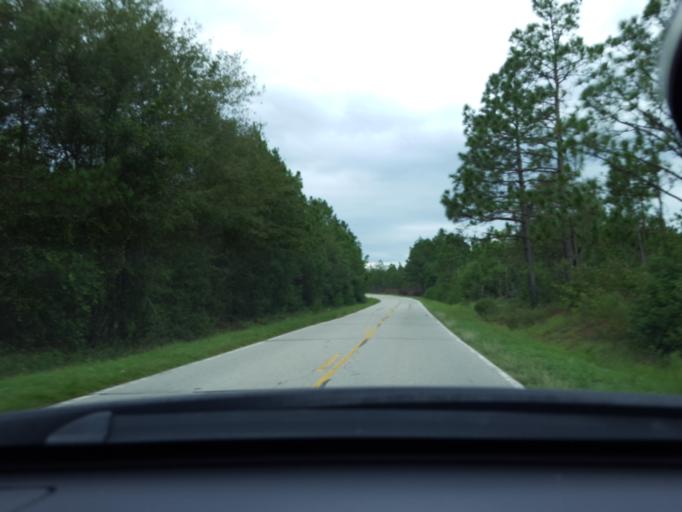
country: US
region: North Carolina
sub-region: Sampson County
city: Clinton
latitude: 34.8006
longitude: -78.2625
